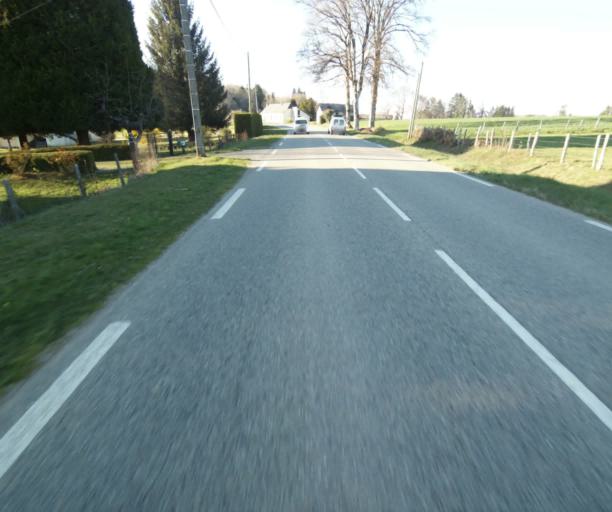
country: FR
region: Limousin
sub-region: Departement de la Correze
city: Seilhac
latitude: 45.3792
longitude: 1.7230
